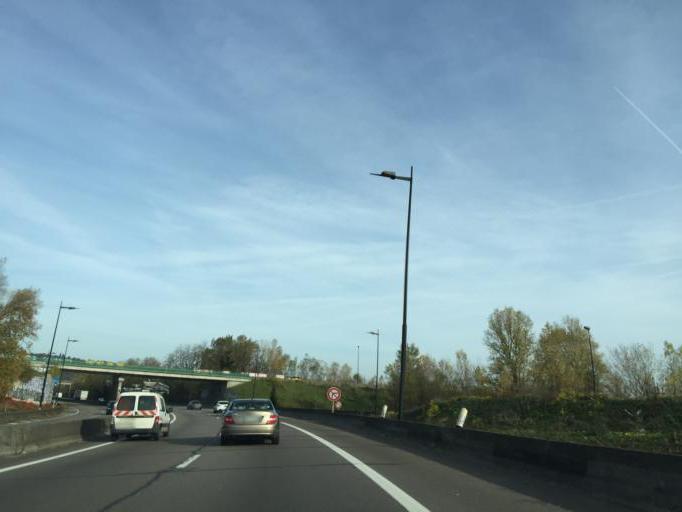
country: FR
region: Rhone-Alpes
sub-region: Departement du Rhone
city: Vaulx-en-Velin
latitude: 45.7969
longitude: 4.9288
